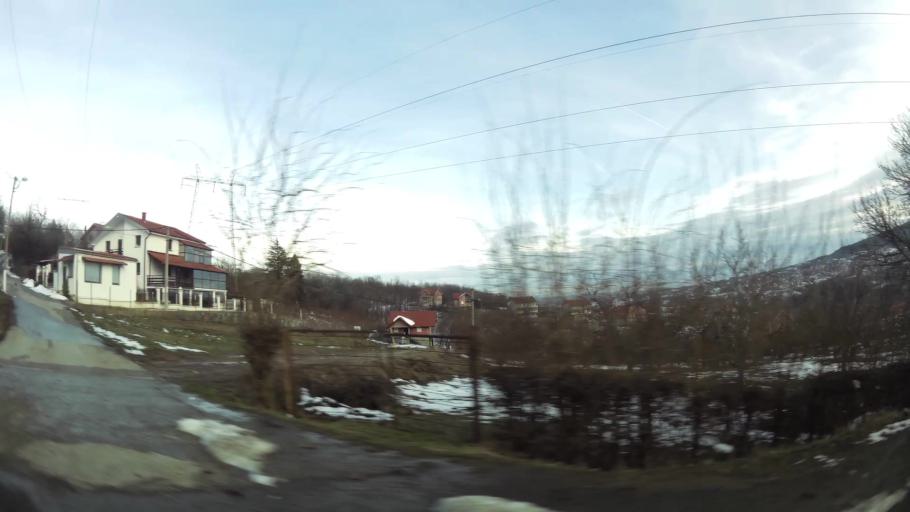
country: RS
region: Central Serbia
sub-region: Belgrade
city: Zvezdara
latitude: 44.7217
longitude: 20.5056
